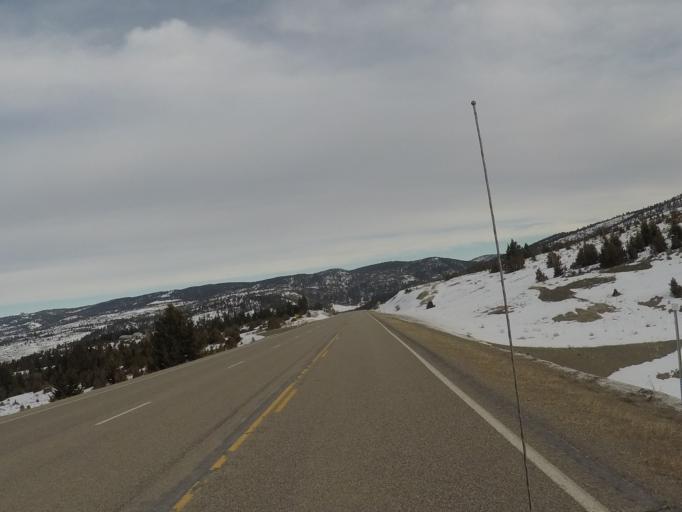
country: US
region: Montana
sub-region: Meagher County
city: White Sulphur Springs
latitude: 46.6557
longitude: -110.8724
